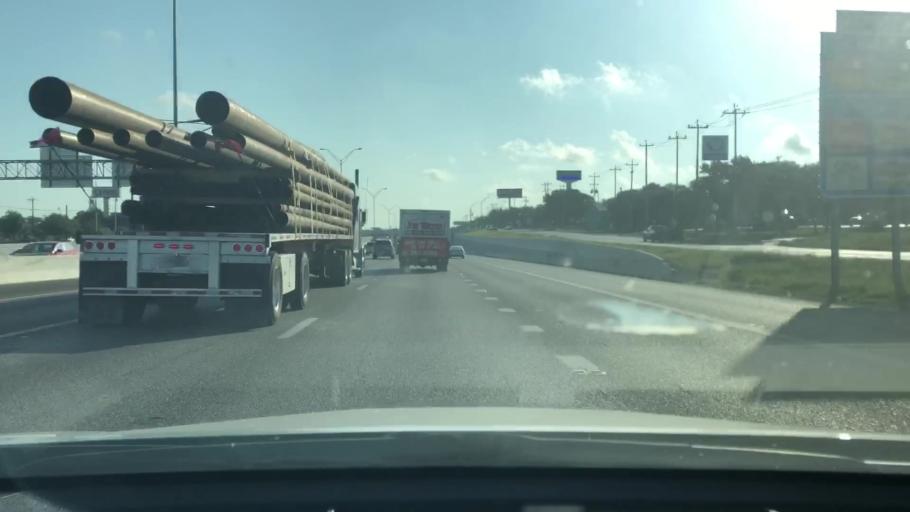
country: US
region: Texas
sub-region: Bexar County
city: Selma
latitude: 29.5911
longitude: -98.2932
